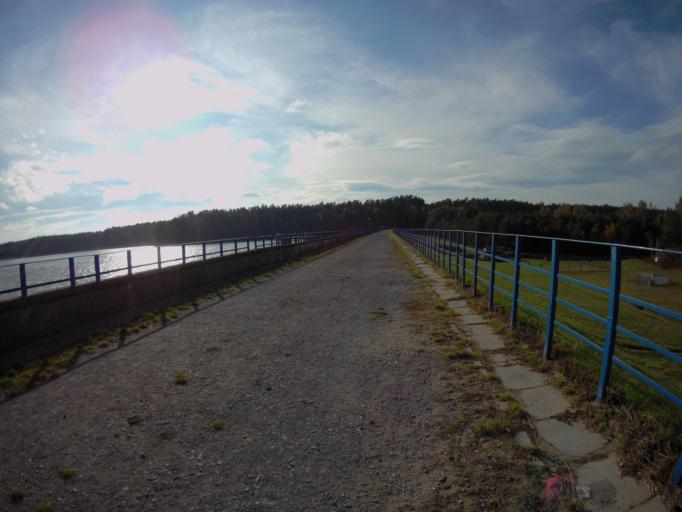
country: PL
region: Subcarpathian Voivodeship
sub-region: Powiat kolbuszowski
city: Lipnica
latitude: 50.3411
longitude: 21.9336
